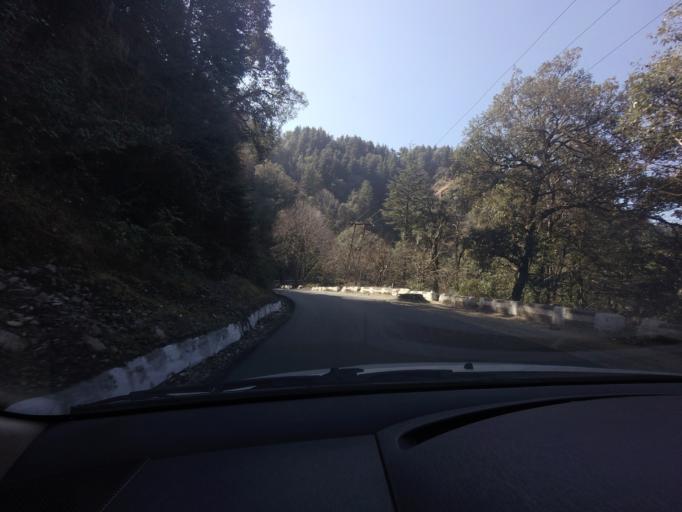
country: IN
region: Himachal Pradesh
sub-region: Shimla
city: Jutogh
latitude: 31.1085
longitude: 77.1061
